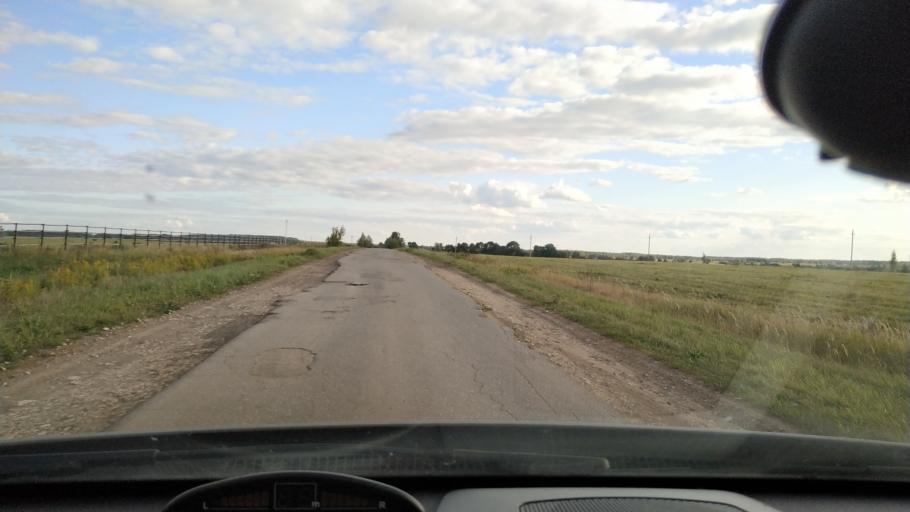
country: RU
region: Rjazan
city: Polyany
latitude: 54.5711
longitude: 39.8620
